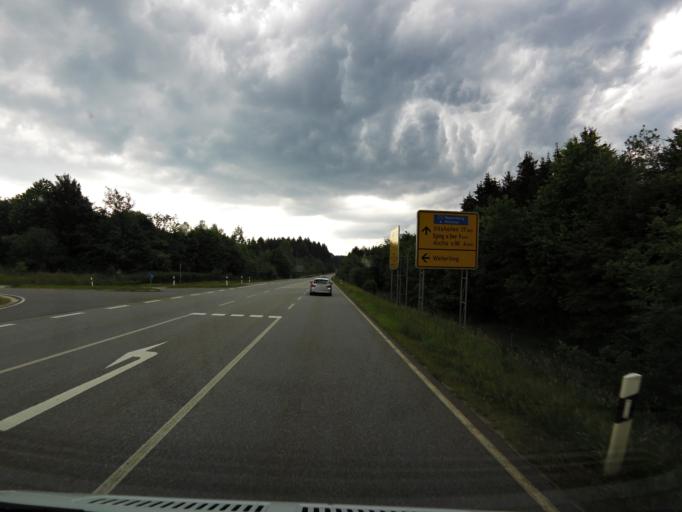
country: DE
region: Bavaria
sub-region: Lower Bavaria
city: Aicha vorm Wald
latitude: 48.6836
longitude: 13.3279
